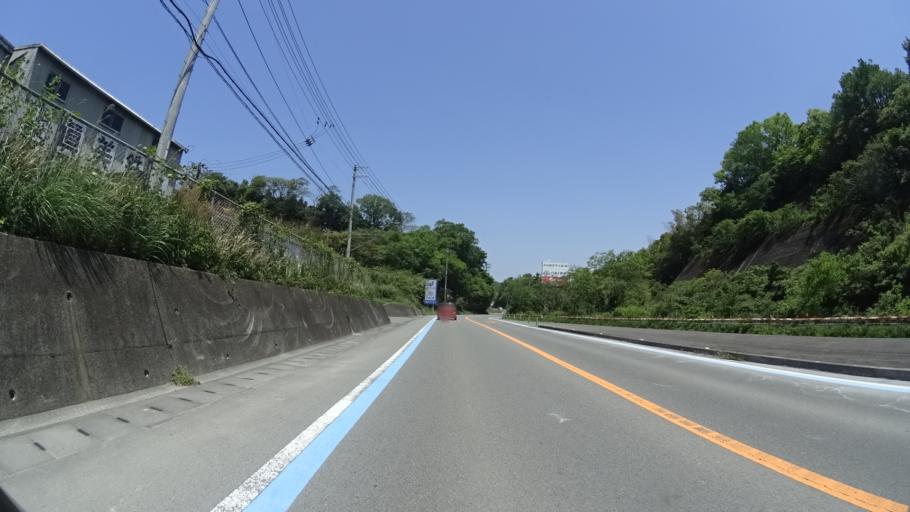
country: JP
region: Ehime
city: Iyo
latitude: 33.7144
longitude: 132.6740
